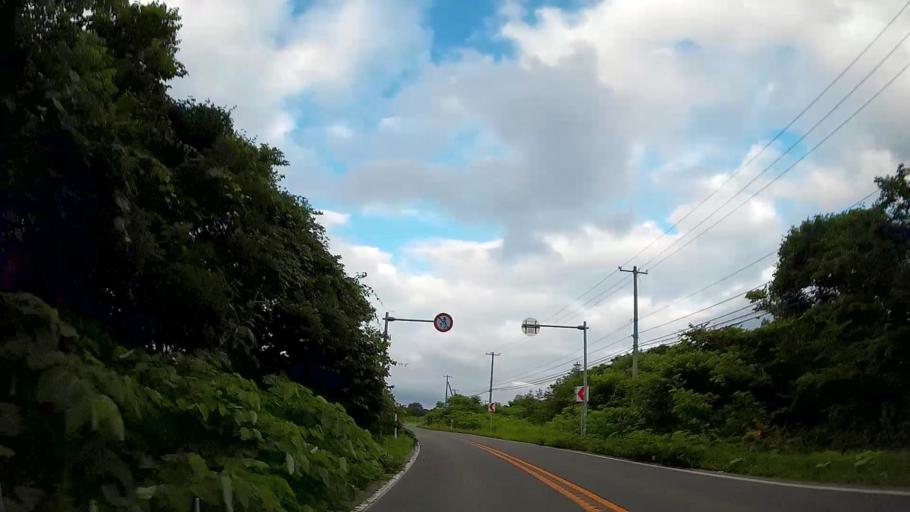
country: JP
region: Hokkaido
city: Nanae
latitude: 42.1153
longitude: 140.7511
